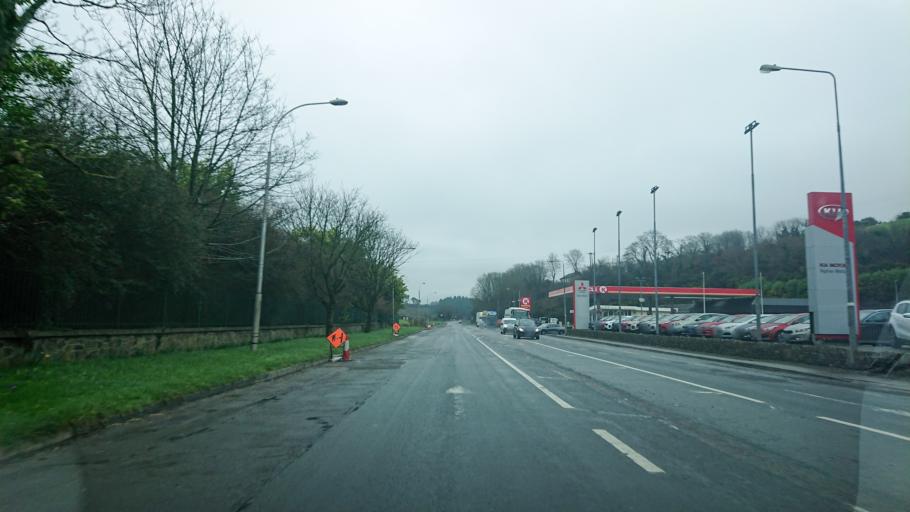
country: IE
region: Munster
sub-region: County Cork
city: Bandon
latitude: 51.7520
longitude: -8.7179
